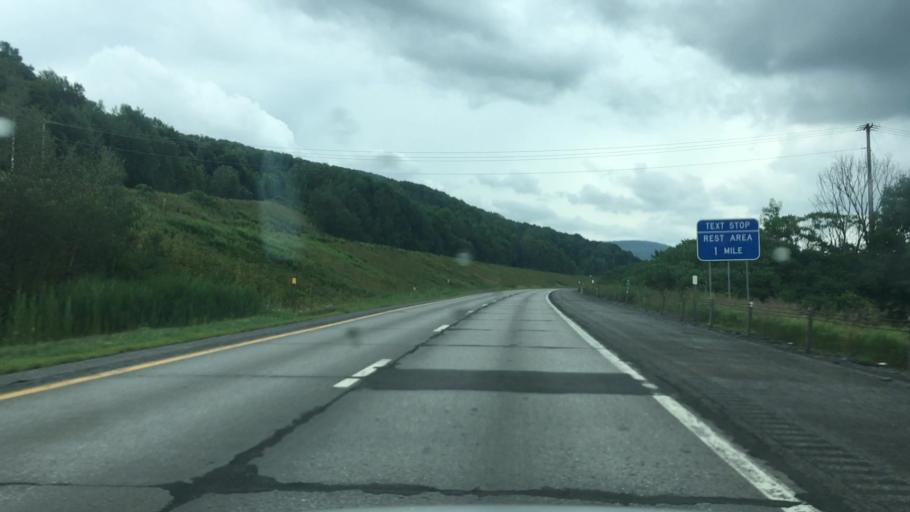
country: US
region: New York
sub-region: Otsego County
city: Worcester
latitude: 42.6204
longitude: -74.6661
